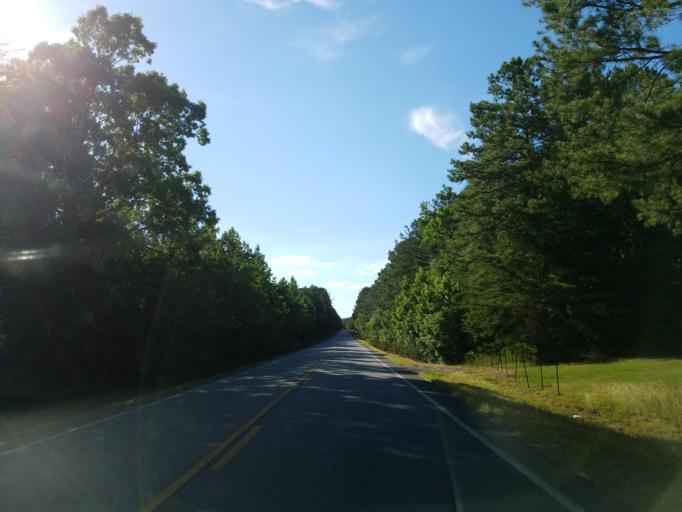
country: US
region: Georgia
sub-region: Gordon County
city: Calhoun
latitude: 34.5811
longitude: -84.9994
